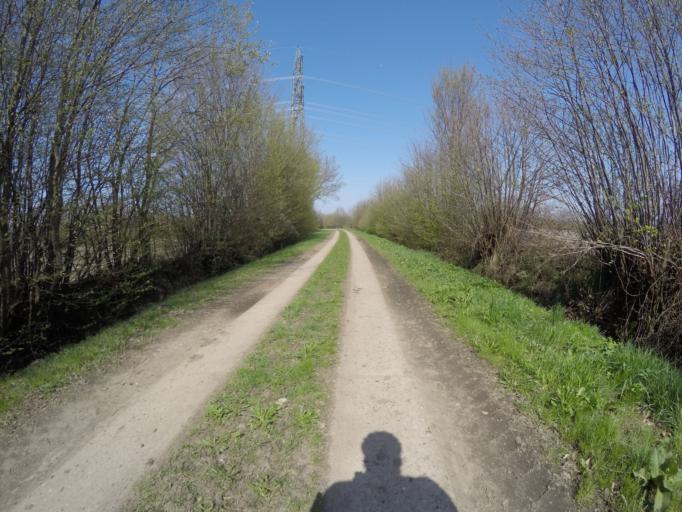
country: DE
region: Schleswig-Holstein
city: Borstel-Hohenraden
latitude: 53.7094
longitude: 9.8395
